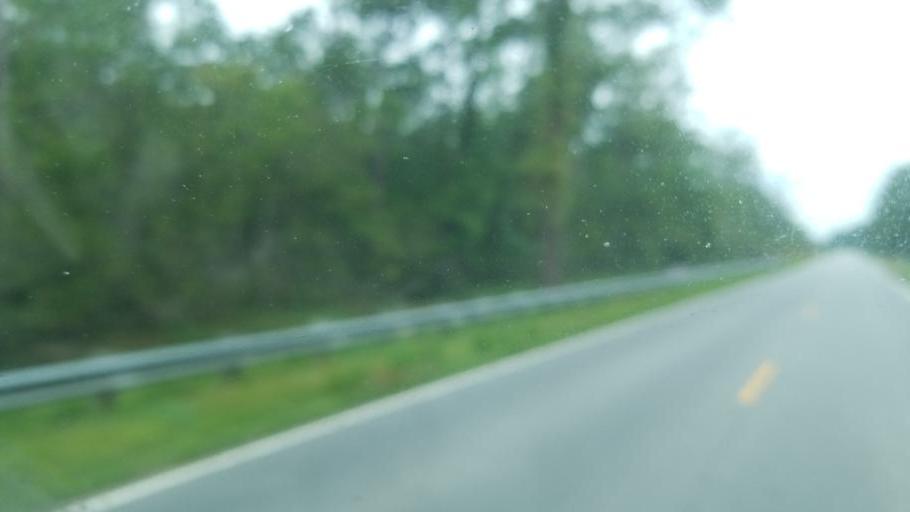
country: US
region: North Carolina
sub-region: Dare County
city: Manteo
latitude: 35.8849
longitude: -75.9526
